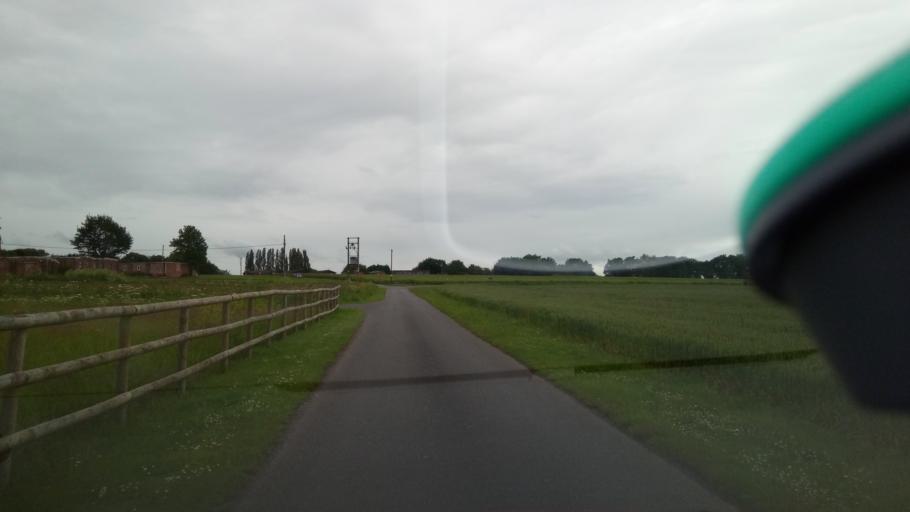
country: GB
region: England
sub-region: Derbyshire
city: Melbourne
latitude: 52.8469
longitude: -1.4164
